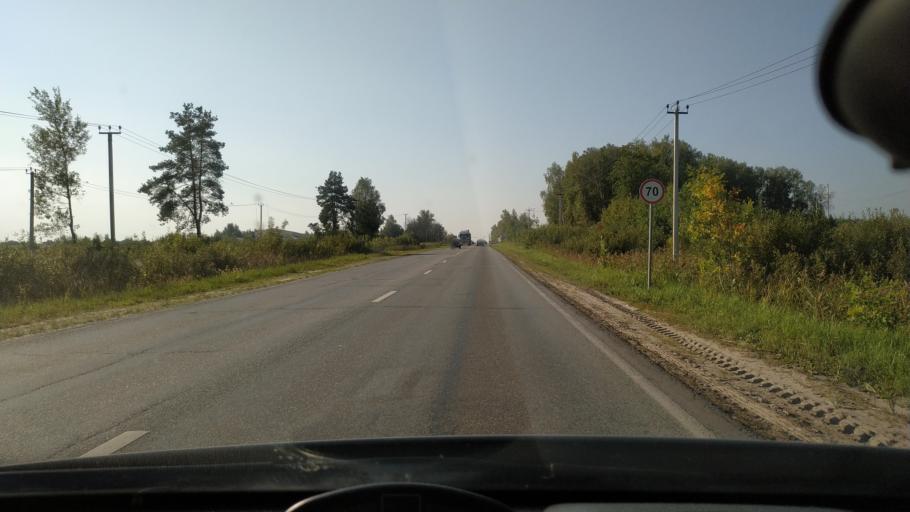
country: RU
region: Moskovskaya
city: Tugolesskiy Bor
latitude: 55.5572
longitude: 39.7026
